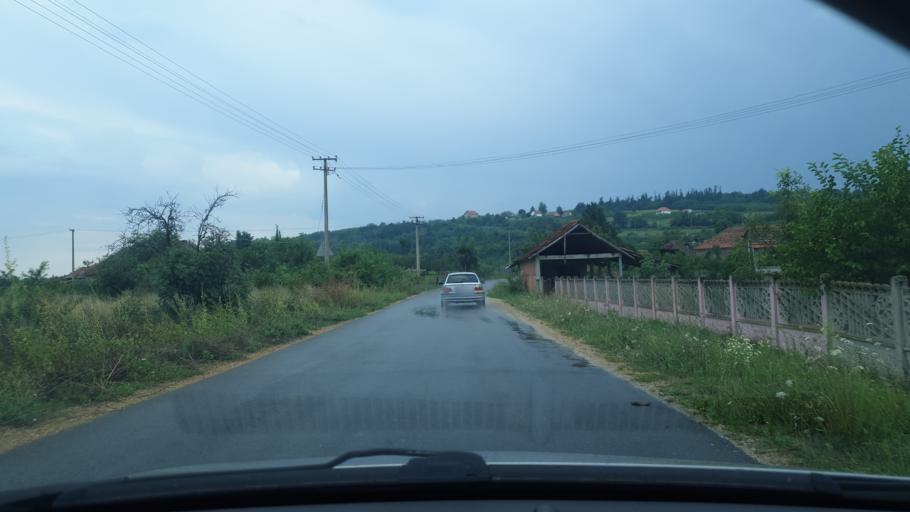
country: RS
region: Central Serbia
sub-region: Sumadijski Okrug
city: Kragujevac
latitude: 44.0640
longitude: 20.7906
